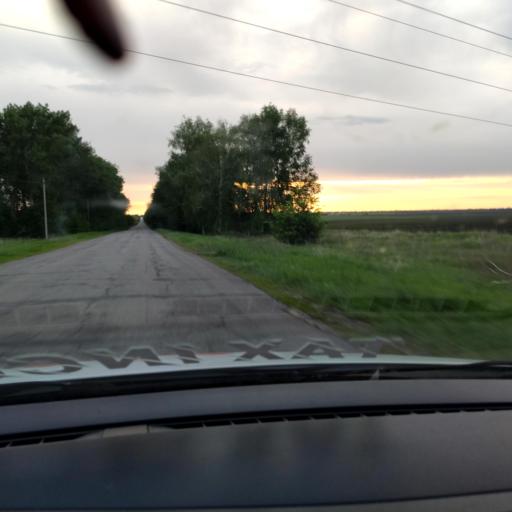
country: RU
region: Voronezj
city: Maslovka
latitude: 51.4417
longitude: 39.2743
